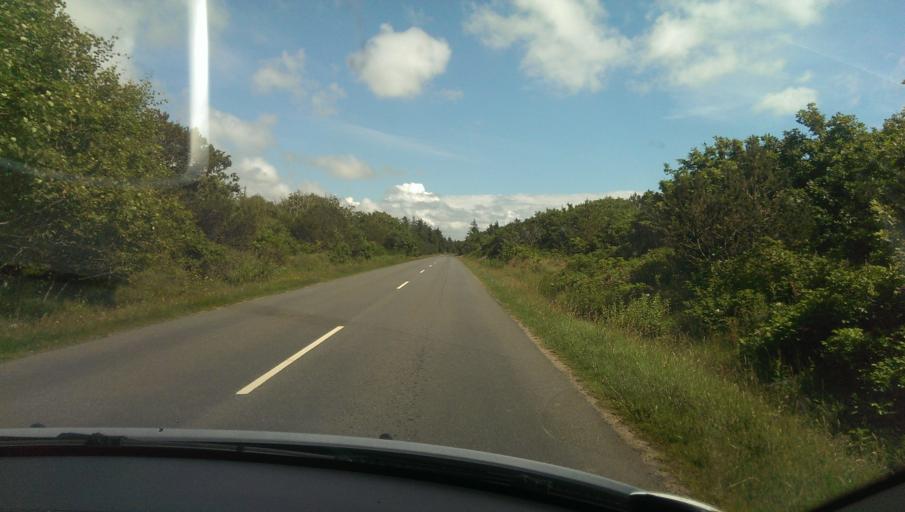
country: DK
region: Central Jutland
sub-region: Ringkobing-Skjern Kommune
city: Ringkobing
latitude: 56.1444
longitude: 8.1384
